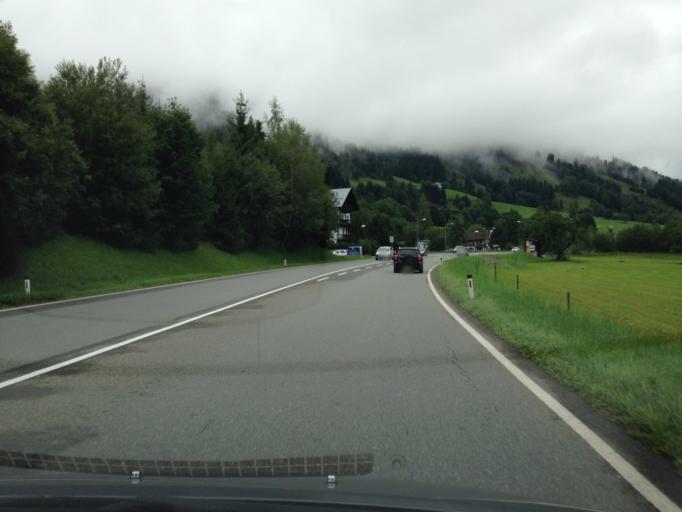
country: AT
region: Salzburg
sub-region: Politischer Bezirk Zell am See
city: Maishofen
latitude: 47.3949
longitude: 12.8005
